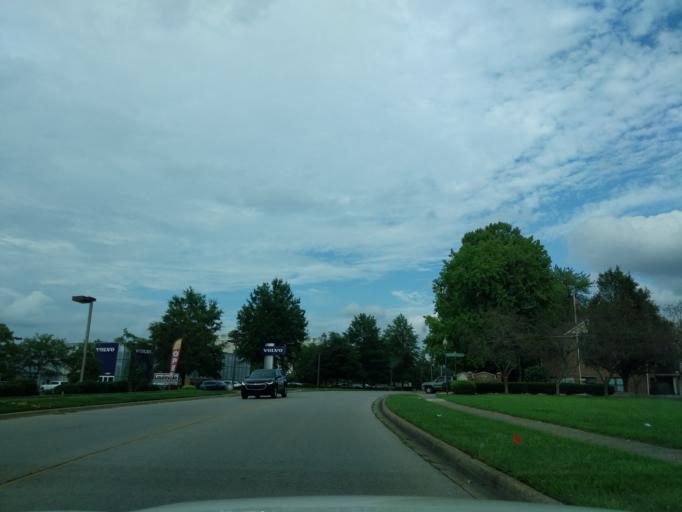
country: US
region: Kentucky
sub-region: Jefferson County
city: Hurstbourne Acres
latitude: 38.2164
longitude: -85.5795
